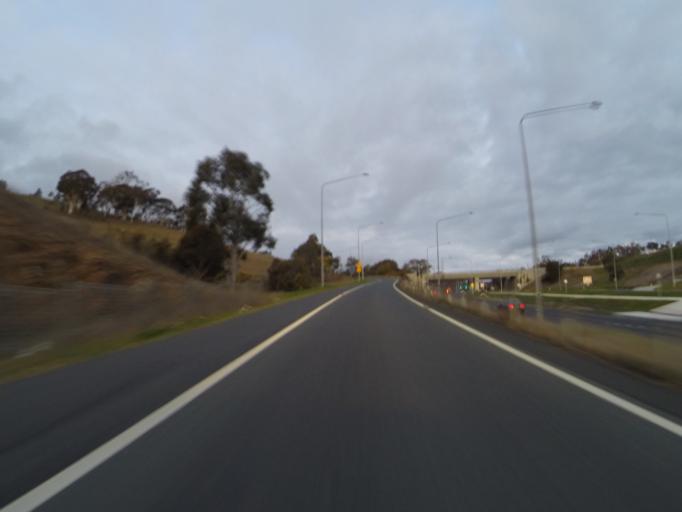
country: AU
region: Australian Capital Territory
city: Kaleen
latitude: -35.2130
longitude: 149.1851
